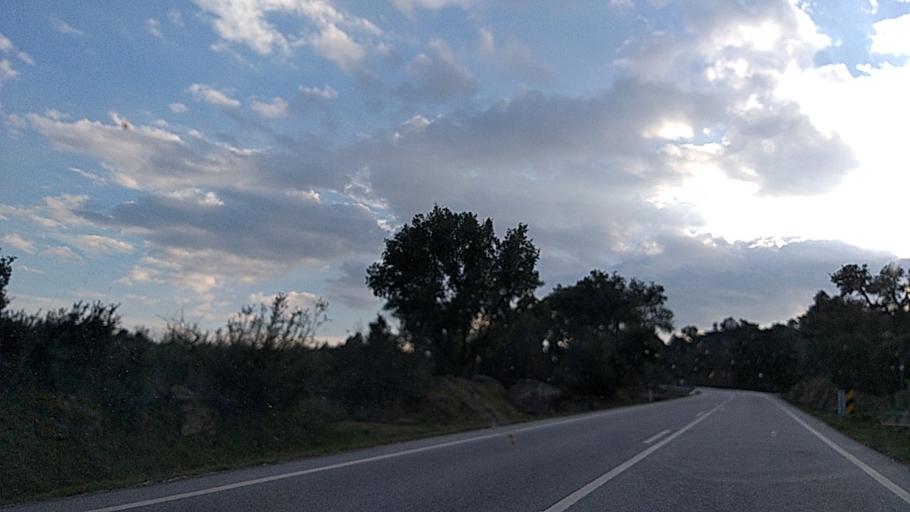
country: ES
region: Castille and Leon
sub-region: Provincia de Salamanca
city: Aldea del Obispo
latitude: 40.6919
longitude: -6.9391
